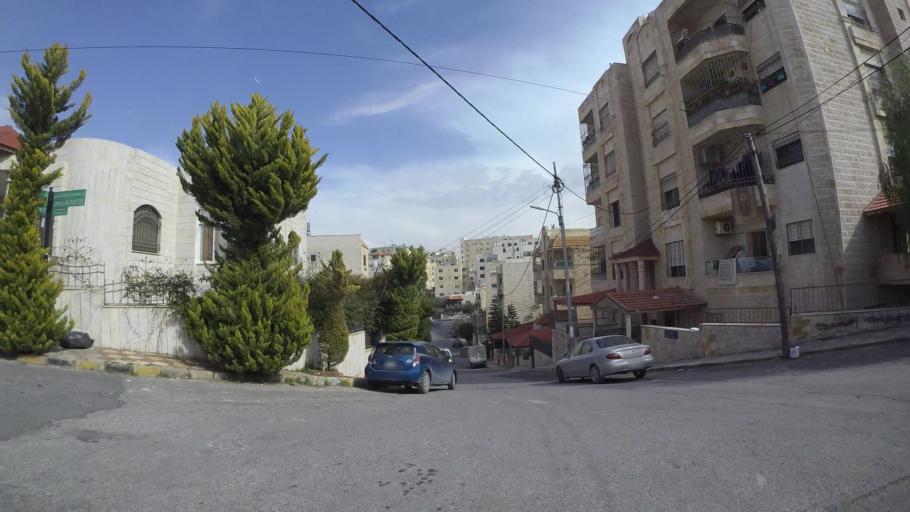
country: JO
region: Amman
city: Amman
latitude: 32.0042
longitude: 35.9377
